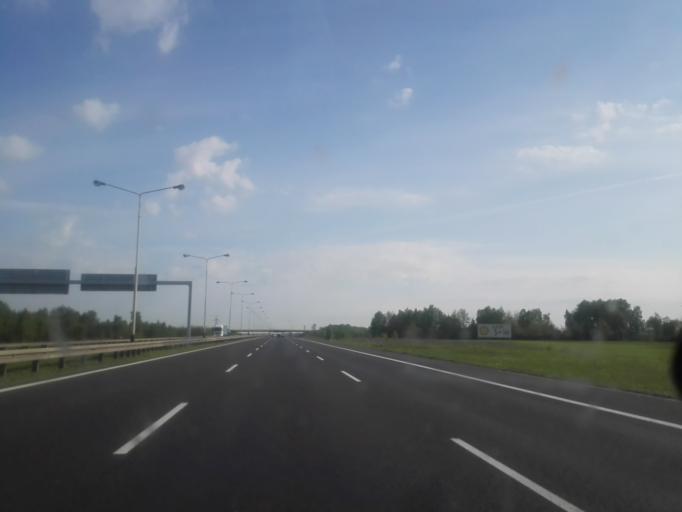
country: PL
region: Lodz Voivodeship
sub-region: Piotrkow Trybunalski
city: Piotrkow Trybunalski
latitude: 51.4214
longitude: 19.6384
